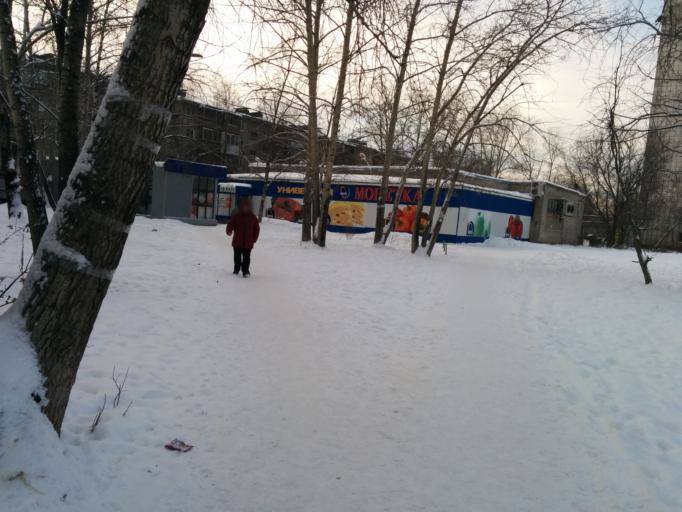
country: RU
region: Perm
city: Perm
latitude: 57.9804
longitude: 56.2922
